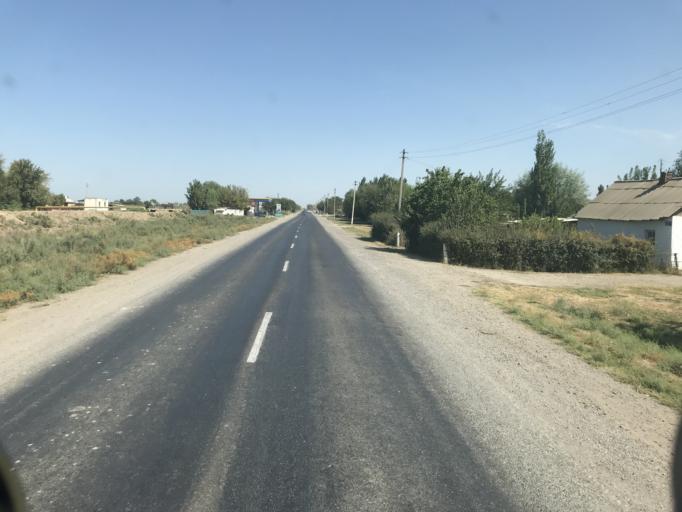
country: KZ
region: Ongtustik Qazaqstan
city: Myrzakent
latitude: 40.7584
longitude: 68.5371
